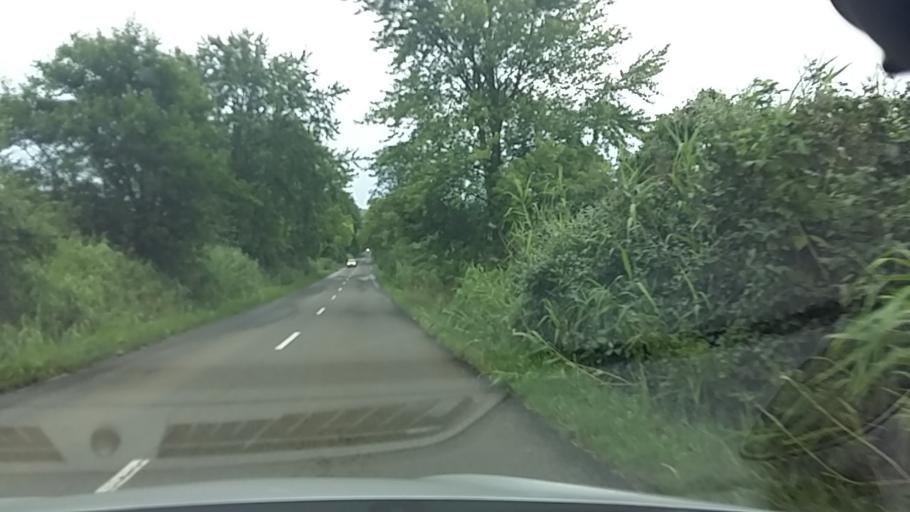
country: HU
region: Komarom-Esztergom
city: Esztergom
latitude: 47.8786
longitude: 18.7817
